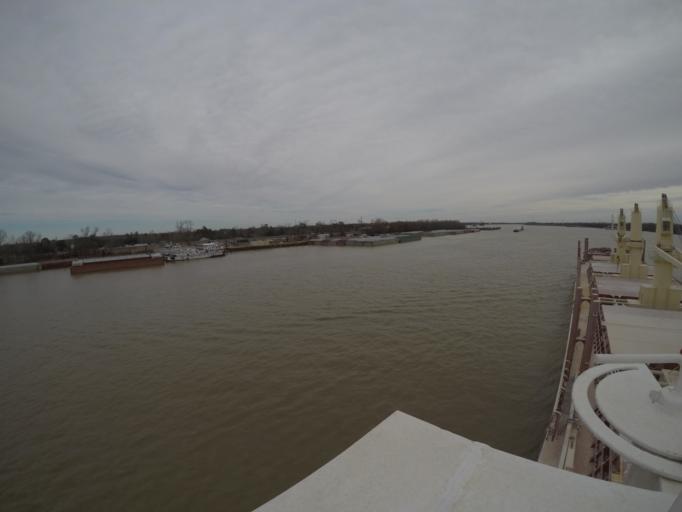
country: US
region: Louisiana
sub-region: Saint John the Baptist Parish
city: Reserve
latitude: 30.0471
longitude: -90.5393
